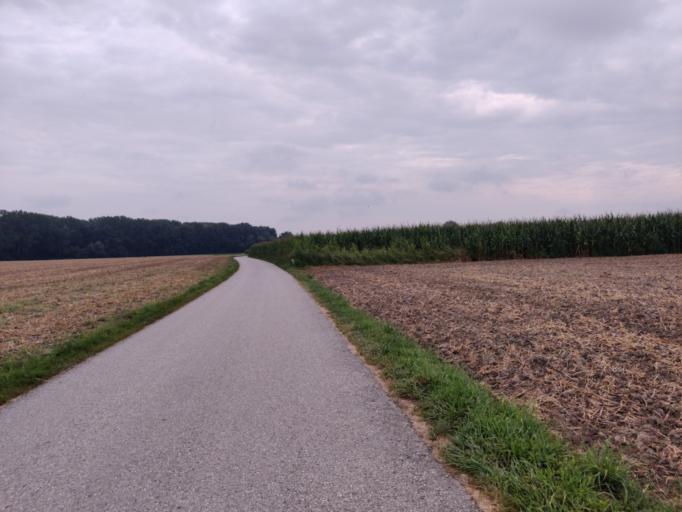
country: AT
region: Upper Austria
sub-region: Politischer Bezirk Linz-Land
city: Asten
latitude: 48.2331
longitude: 14.4394
